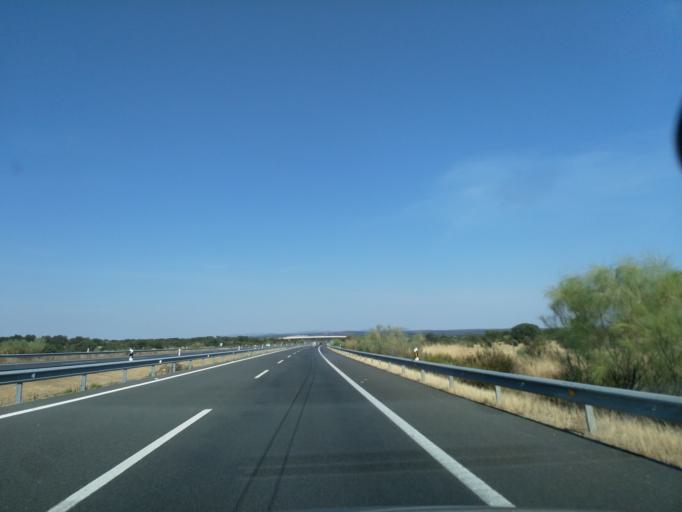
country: ES
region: Extremadura
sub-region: Provincia de Caceres
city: Alcuescar
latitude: 39.1853
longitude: -6.2758
